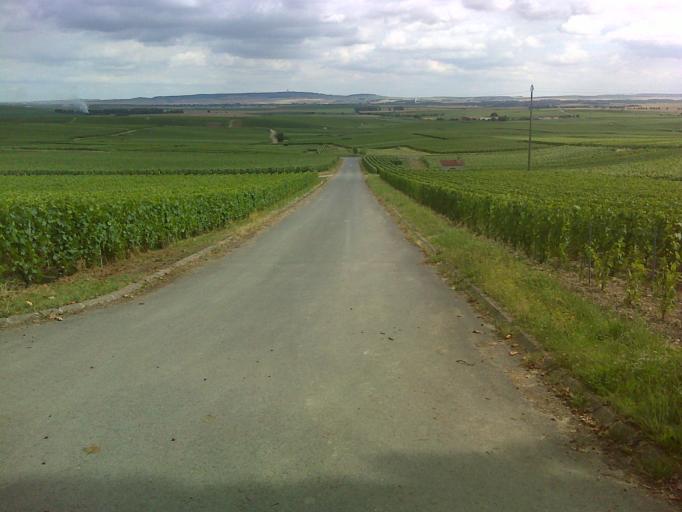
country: FR
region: Champagne-Ardenne
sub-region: Departement de la Marne
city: Rilly-la-Montagne
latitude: 49.1587
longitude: 4.0539
